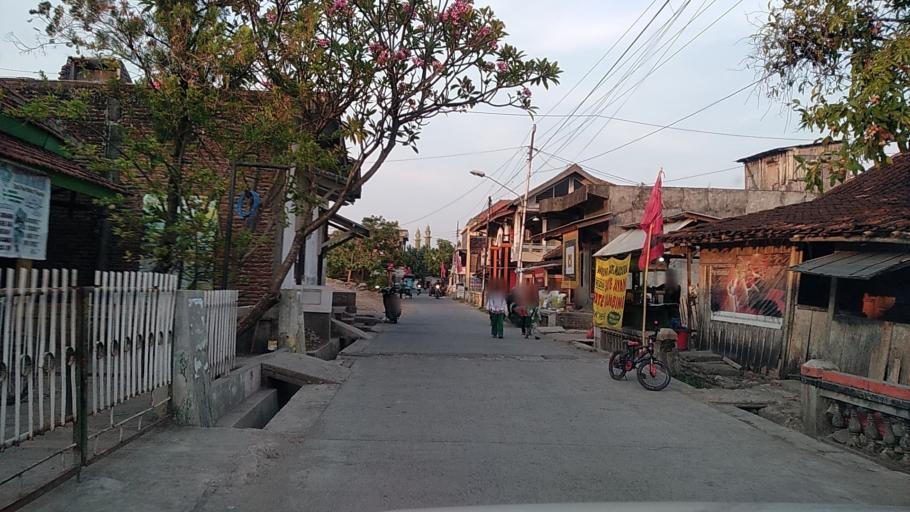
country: ID
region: Central Java
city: Semarang
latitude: -6.9569
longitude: 110.3135
